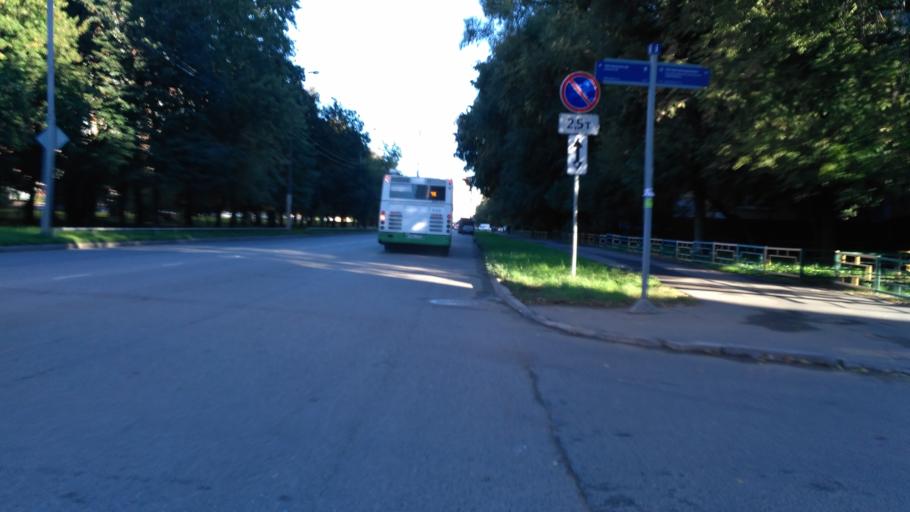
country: RU
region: Moskovskaya
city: Vostochnoe Degunino
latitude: 55.8656
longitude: 37.5596
